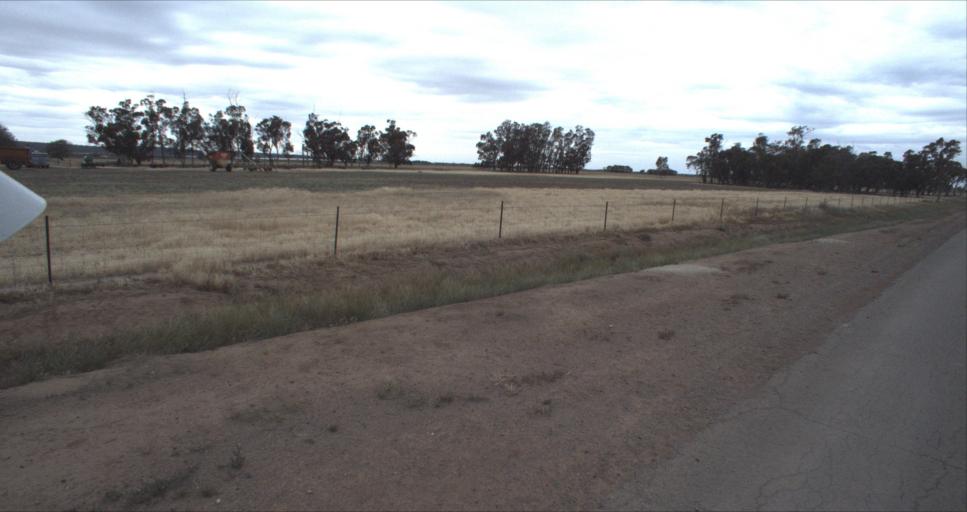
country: AU
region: New South Wales
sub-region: Leeton
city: Leeton
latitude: -34.4070
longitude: 146.3410
